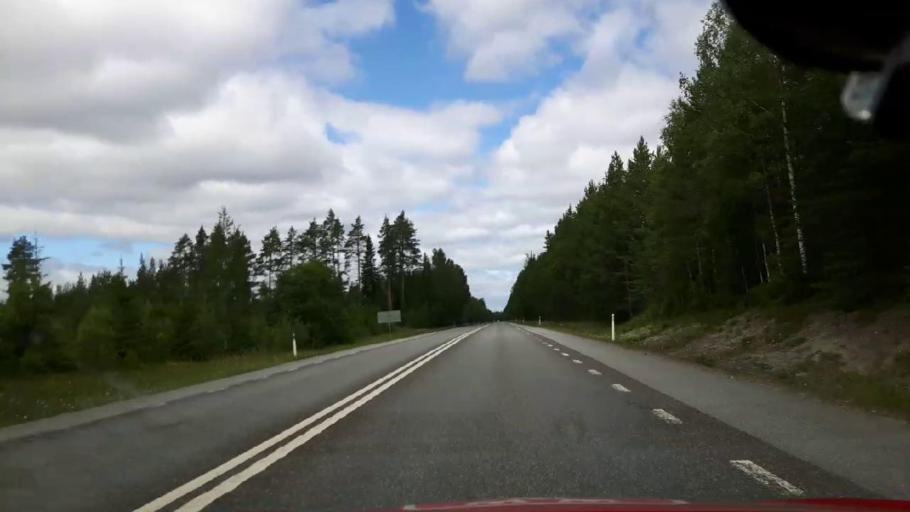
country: SE
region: Jaemtland
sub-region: Braecke Kommun
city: Braecke
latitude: 62.7200
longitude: 15.4519
